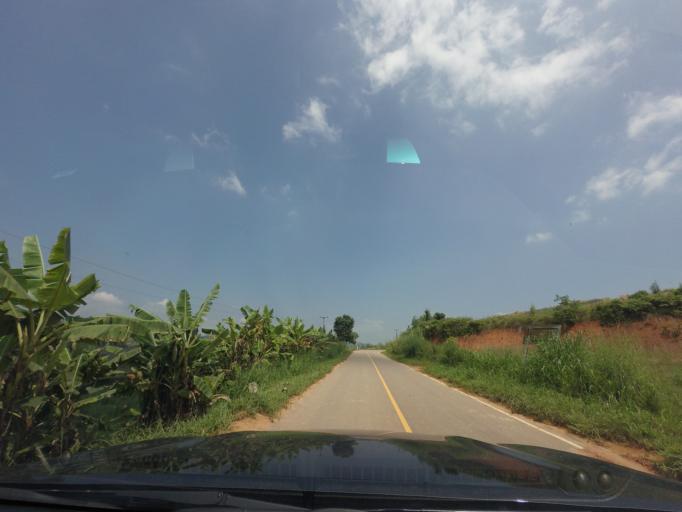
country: TH
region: Loei
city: Na Haeo
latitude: 17.5250
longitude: 100.8776
